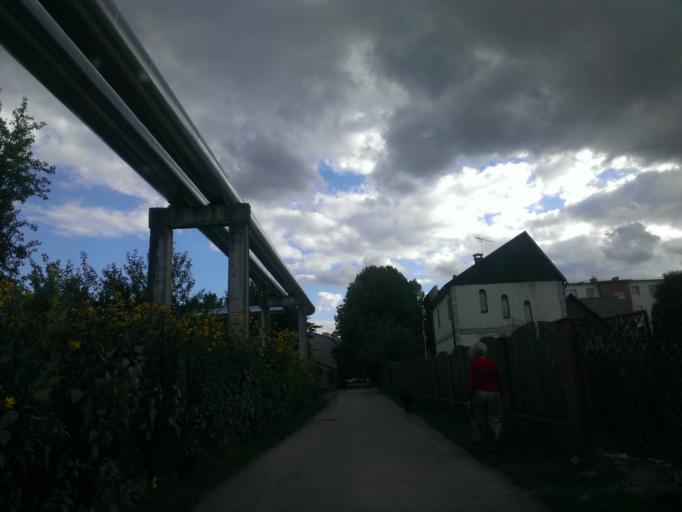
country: LV
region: Sigulda
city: Sigulda
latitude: 57.1552
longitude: 24.8791
